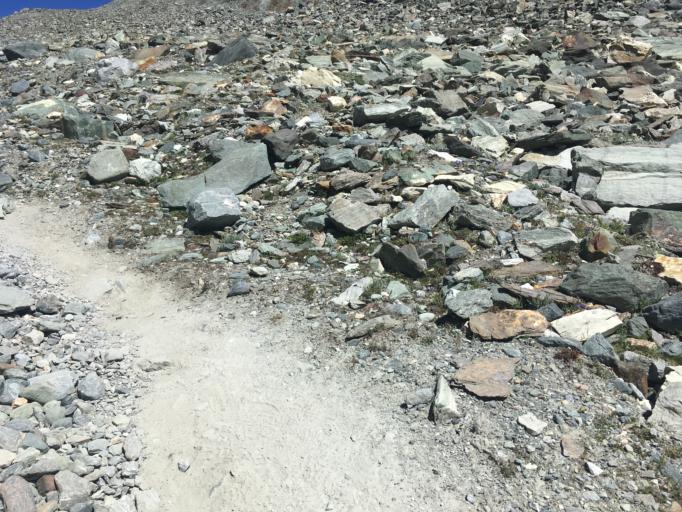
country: CH
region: Valais
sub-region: Visp District
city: Zermatt
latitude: 45.9853
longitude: 7.6937
